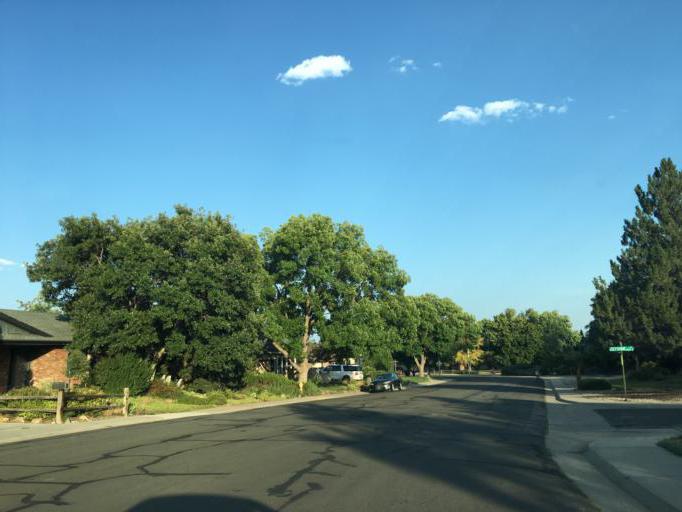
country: US
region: Colorado
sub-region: Jefferson County
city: Applewood
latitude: 39.7950
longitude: -105.1549
